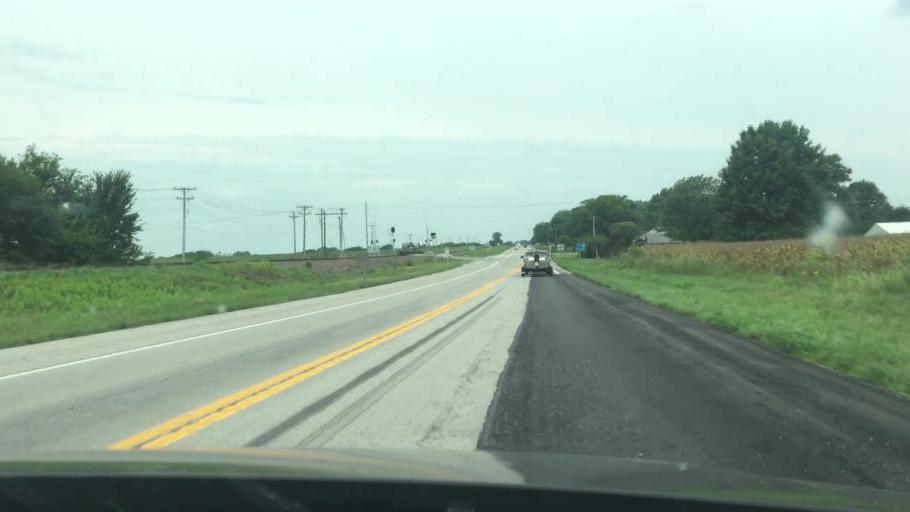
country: US
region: Missouri
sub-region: Pettis County
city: Sedalia
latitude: 38.6951
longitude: -93.1505
